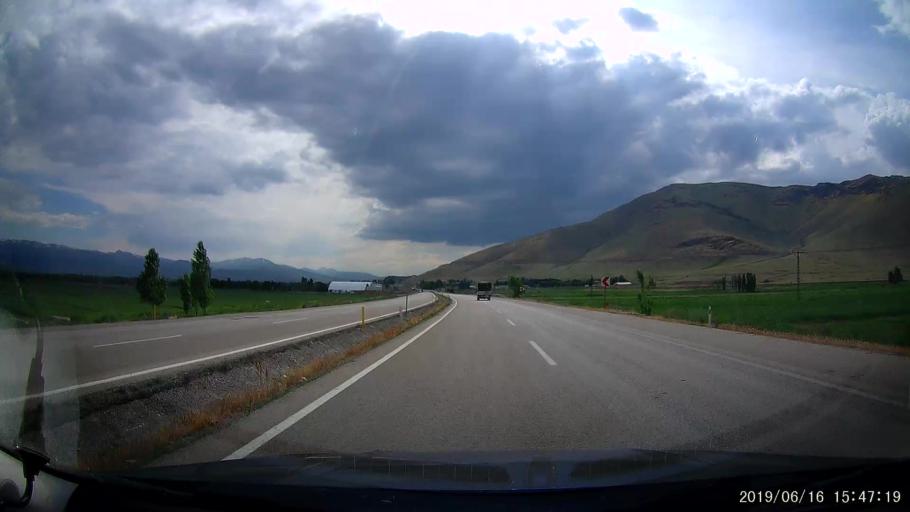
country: TR
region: Erzurum
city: Pasinler
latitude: 39.9888
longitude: 41.7236
